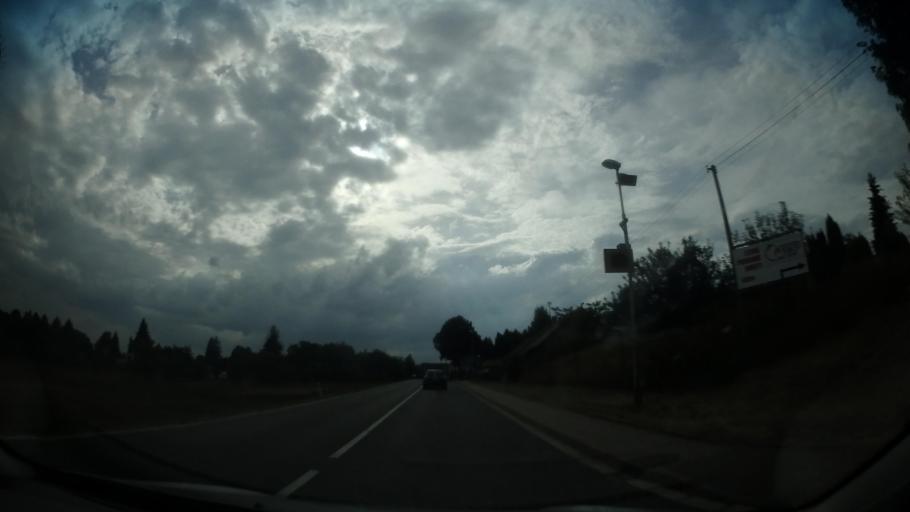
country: CZ
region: Pardubicky
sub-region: Okres Chrudim
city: Sec
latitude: 49.8491
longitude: 15.6646
